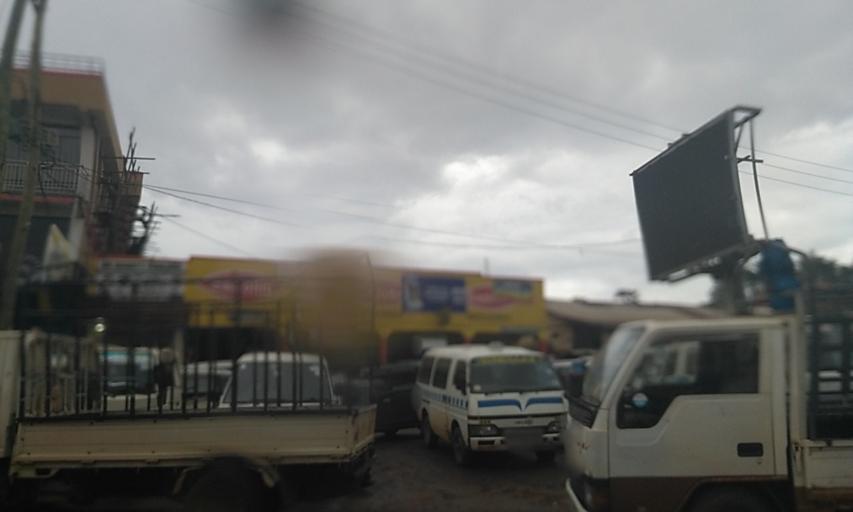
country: UG
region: Central Region
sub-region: Wakiso District
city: Kireka
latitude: 0.3465
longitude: 32.6488
